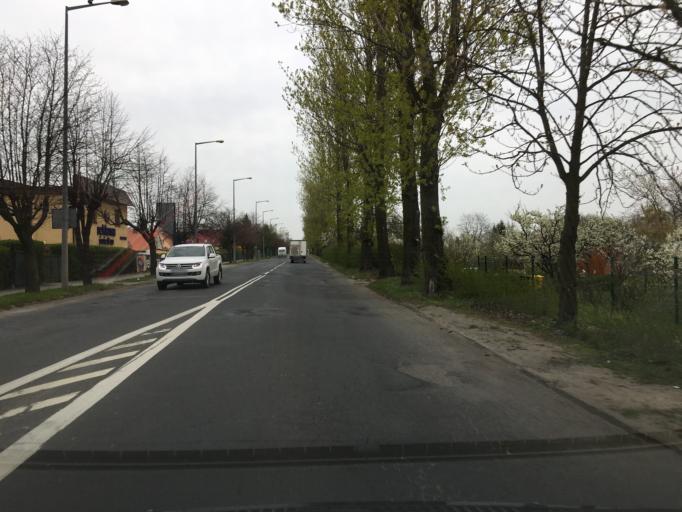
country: PL
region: Lower Silesian Voivodeship
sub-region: Legnica
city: Legnica
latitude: 51.1894
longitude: 16.1691
